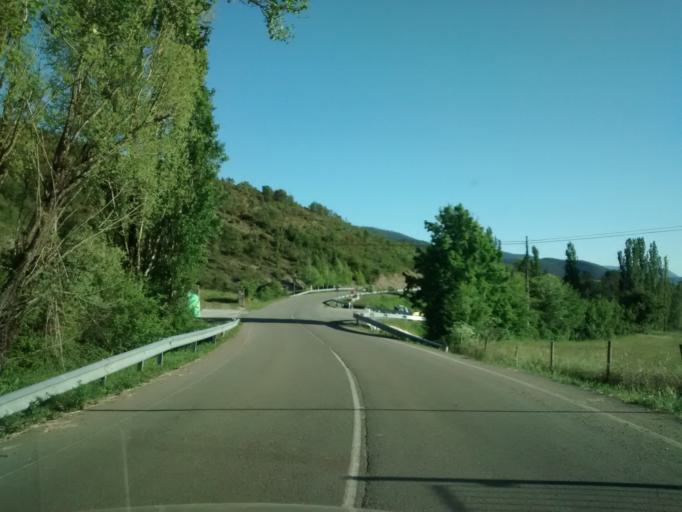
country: ES
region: Aragon
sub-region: Provincia de Huesca
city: Borau
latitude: 42.6790
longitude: -0.6192
